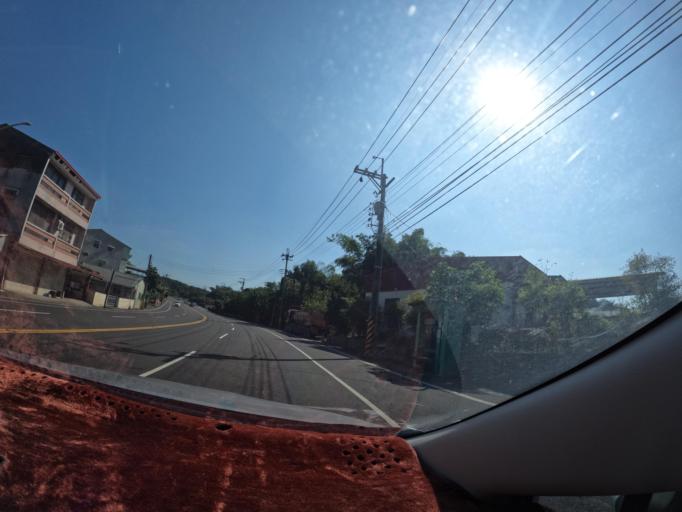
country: TW
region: Taiwan
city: Yujing
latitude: 23.0652
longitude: 120.3823
